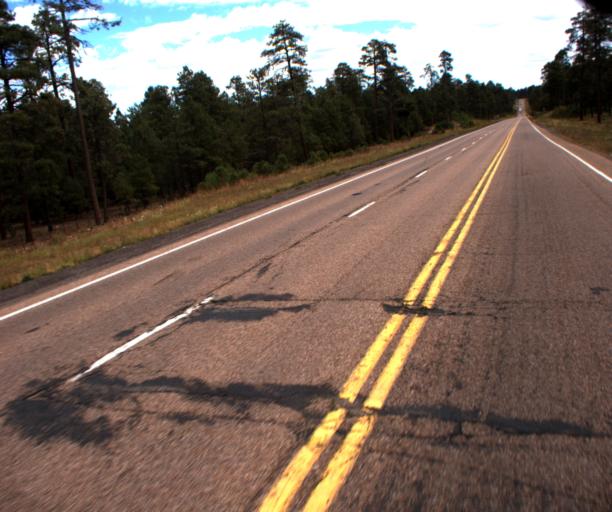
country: US
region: Arizona
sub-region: Navajo County
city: Heber-Overgaard
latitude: 34.3352
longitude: -110.7462
